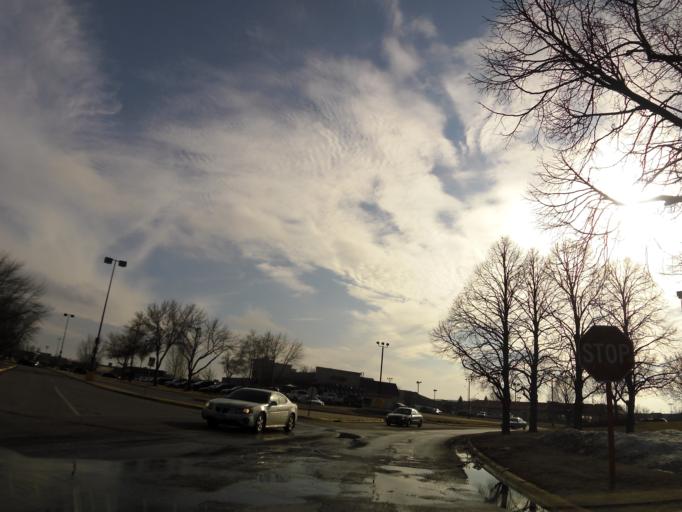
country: US
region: North Dakota
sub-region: Grand Forks County
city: Grand Forks
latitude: 47.8908
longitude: -97.0688
